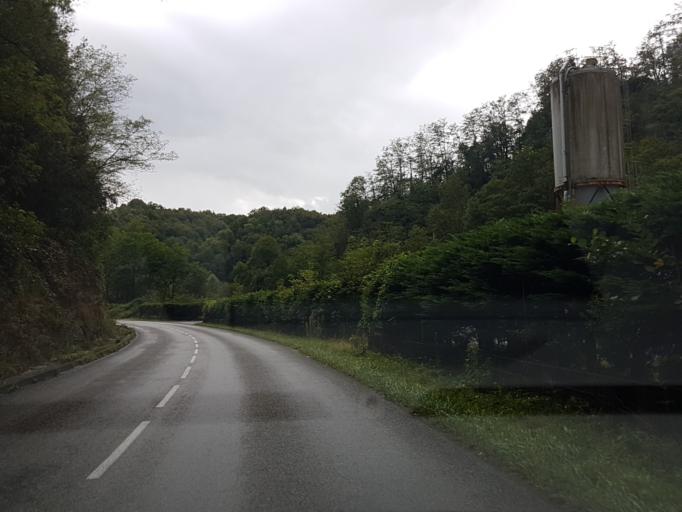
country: FR
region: Midi-Pyrenees
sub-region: Departement de l'Ariege
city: Saint-Girons
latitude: 42.9050
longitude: 1.2113
